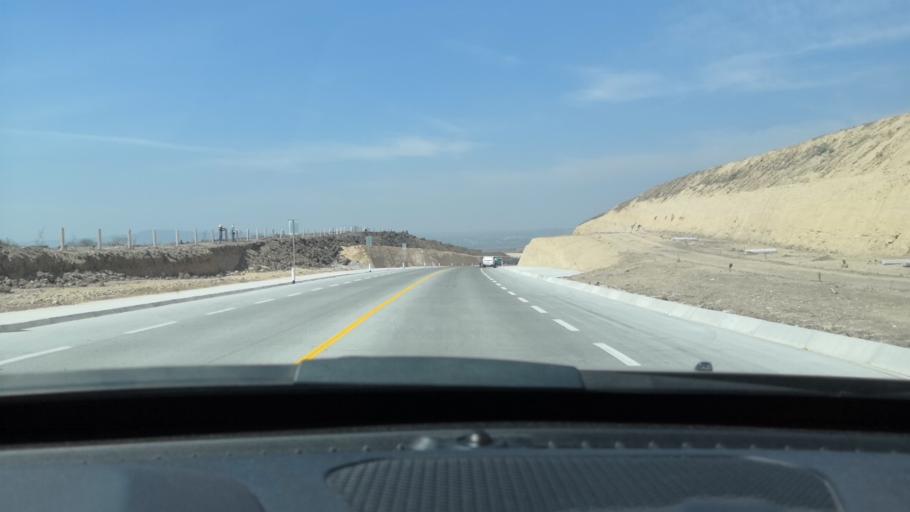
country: MX
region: Guanajuato
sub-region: San Francisco del Rincon
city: Estacion de San Francisco
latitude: 21.0874
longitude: -101.7991
